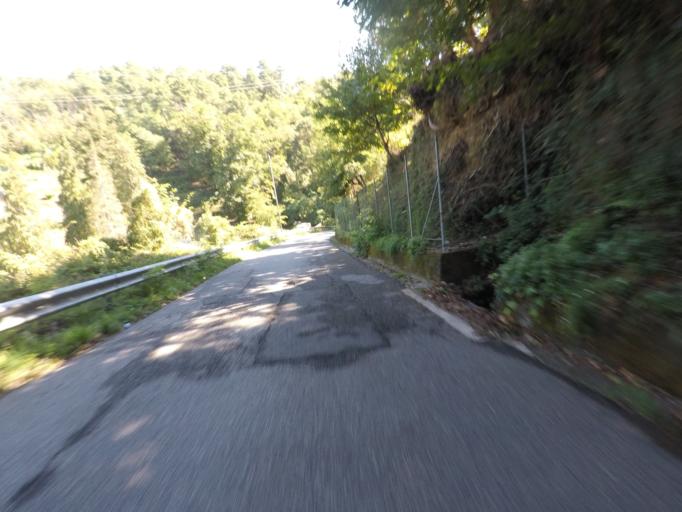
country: IT
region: Tuscany
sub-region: Provincia di Massa-Carrara
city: Montignoso
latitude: 44.0401
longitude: 10.1567
